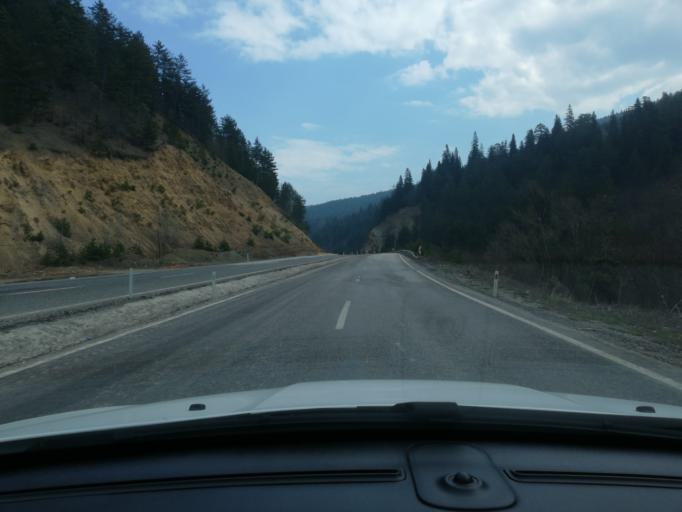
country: TR
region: Kastamonu
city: Kuzyaka
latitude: 41.1522
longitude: 33.7860
